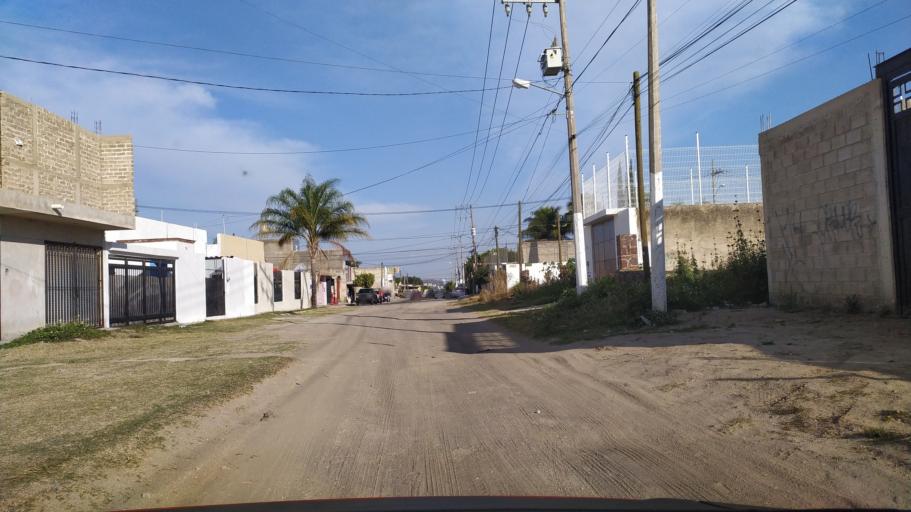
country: MX
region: Jalisco
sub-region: Tlajomulco de Zuniga
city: Palomar
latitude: 20.6288
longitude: -103.4745
